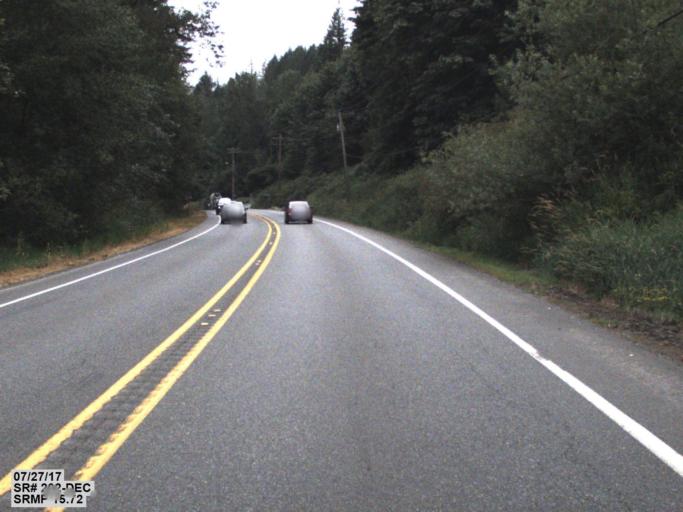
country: US
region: Washington
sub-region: King County
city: Ames Lake
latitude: 47.6215
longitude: -121.9621
